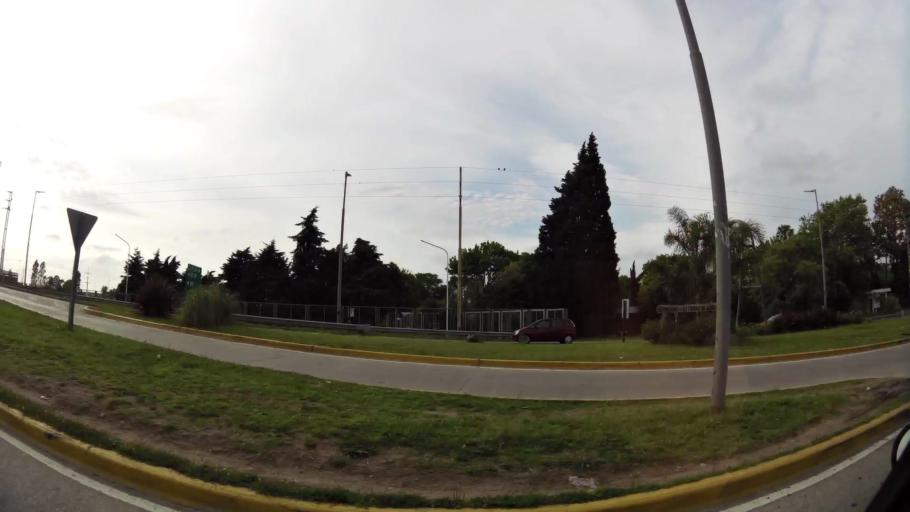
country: AR
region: Buenos Aires
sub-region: Partido de Quilmes
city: Quilmes
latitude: -34.7029
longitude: -58.2760
